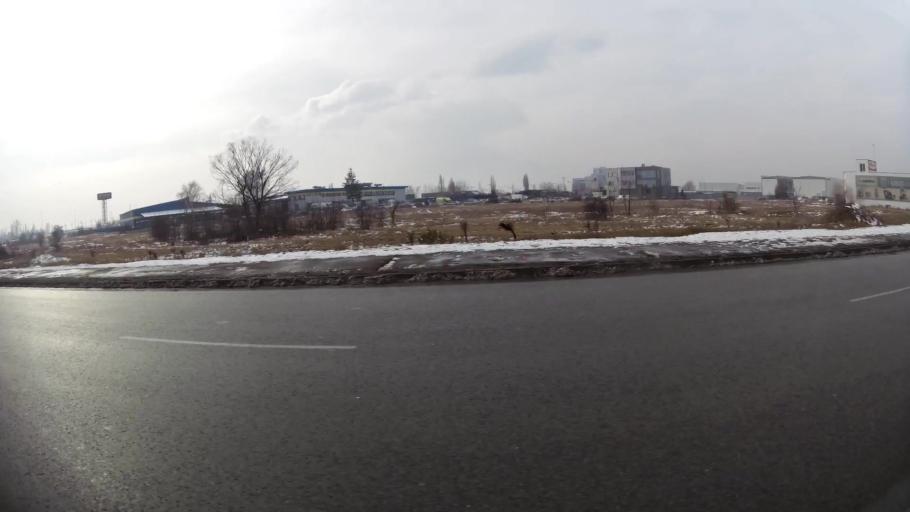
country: BG
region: Sofia-Capital
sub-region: Stolichna Obshtina
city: Sofia
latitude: 42.7081
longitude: 23.4003
